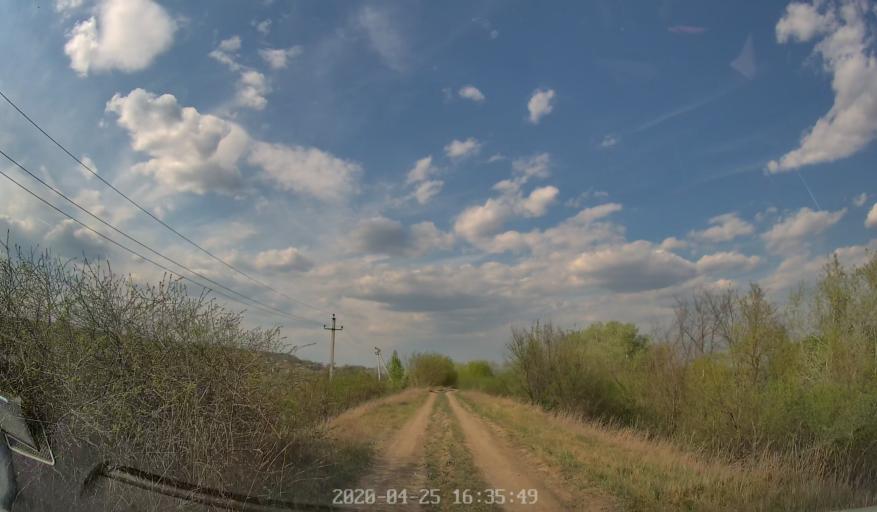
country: MD
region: Chisinau
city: Vadul lui Voda
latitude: 47.1101
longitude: 29.0643
